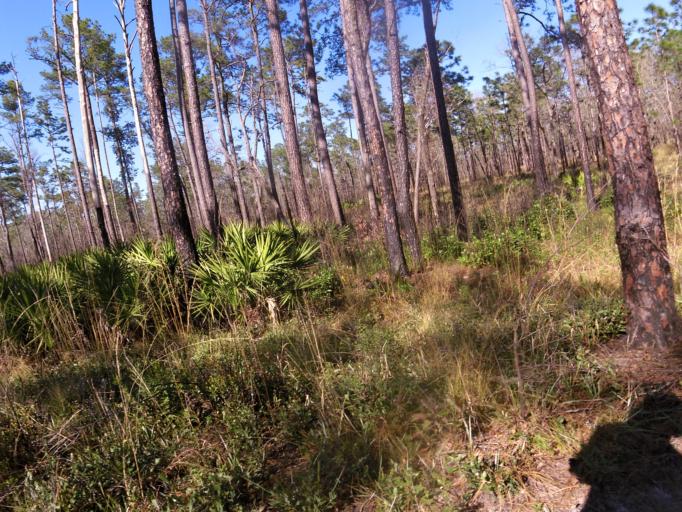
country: US
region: Florida
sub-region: Clay County
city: Middleburg
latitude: 30.1409
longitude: -81.8870
